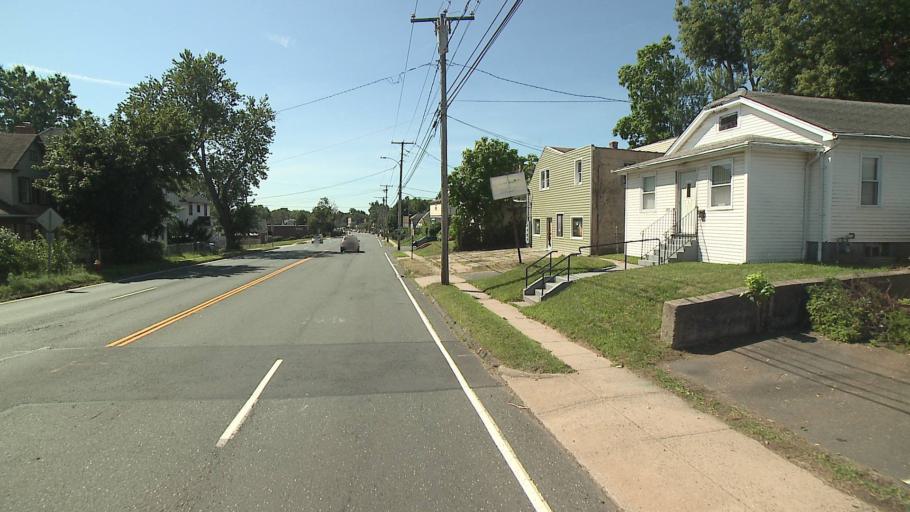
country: US
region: Connecticut
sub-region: Hartford County
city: Blue Hills
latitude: 41.8088
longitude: -72.6955
